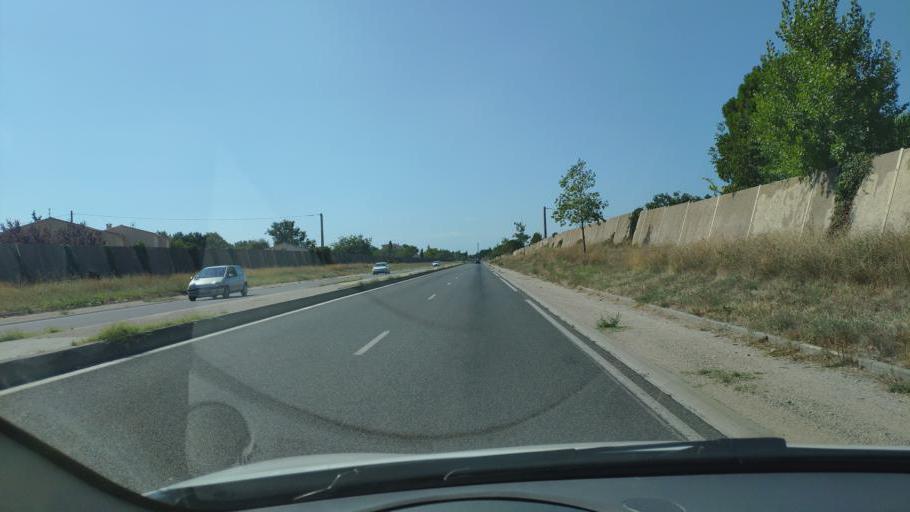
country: FR
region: Provence-Alpes-Cote d'Azur
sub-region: Departement du Vaucluse
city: Carpentras
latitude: 44.0676
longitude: 5.0636
